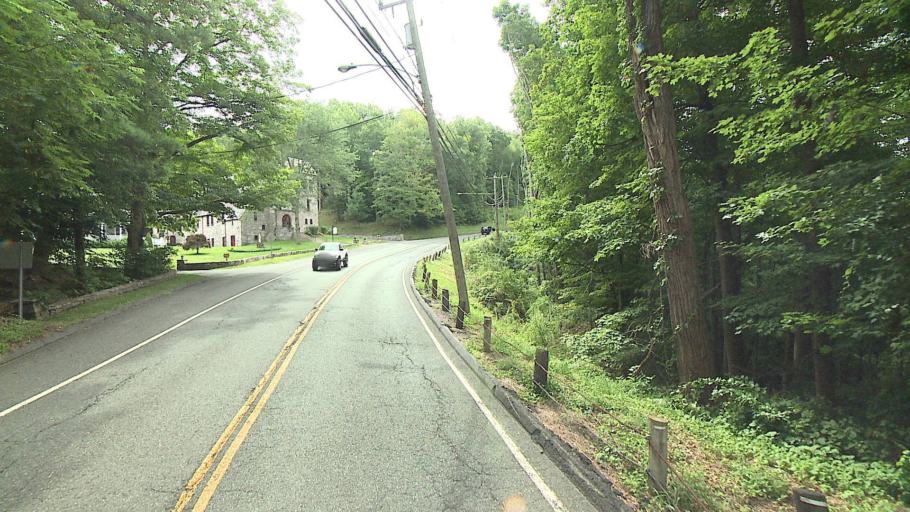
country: US
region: Connecticut
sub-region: Litchfield County
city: New Preston
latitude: 41.6370
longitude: -73.3164
